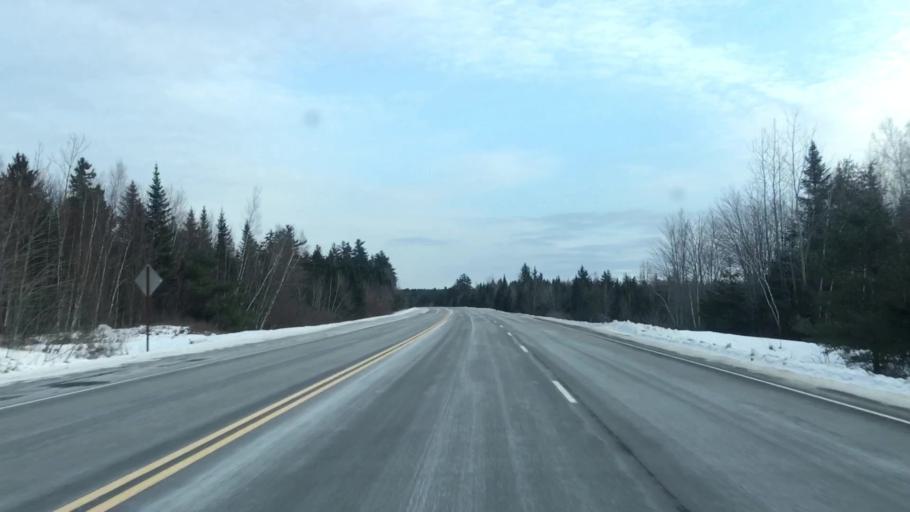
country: US
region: Maine
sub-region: Washington County
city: Addison
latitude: 44.9108
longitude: -67.7974
